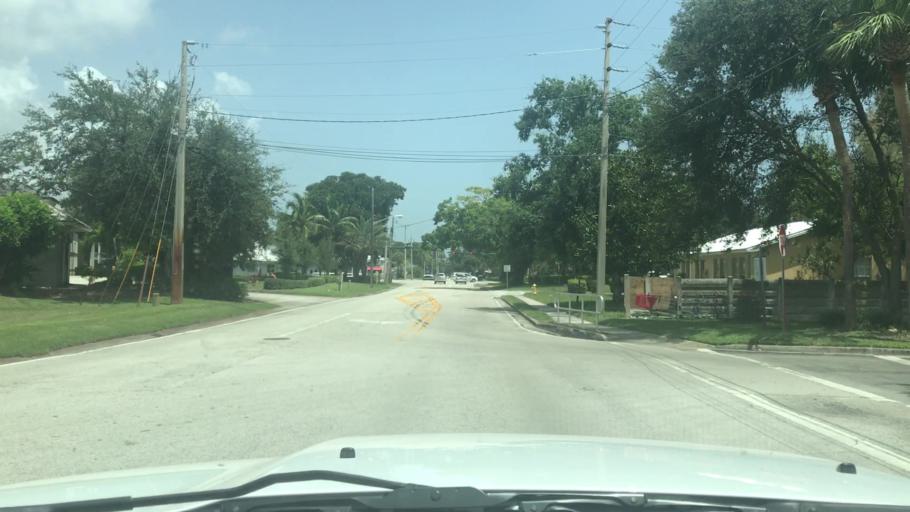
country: US
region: Florida
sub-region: Indian River County
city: Vero Beach
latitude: 27.6310
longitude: -80.3932
